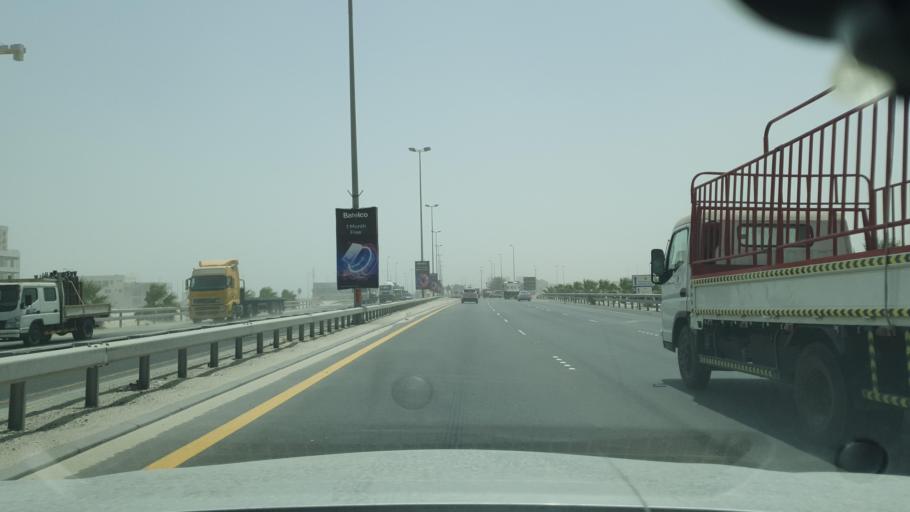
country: BH
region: Muharraq
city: Al Hadd
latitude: 26.2249
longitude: 50.6535
